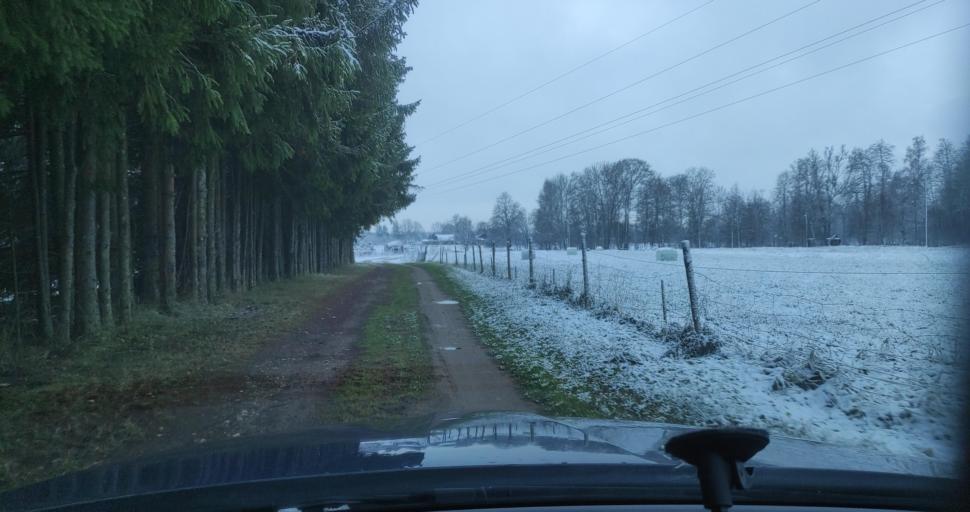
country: LV
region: Skrunda
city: Skrunda
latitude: 56.8749
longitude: 22.2331
